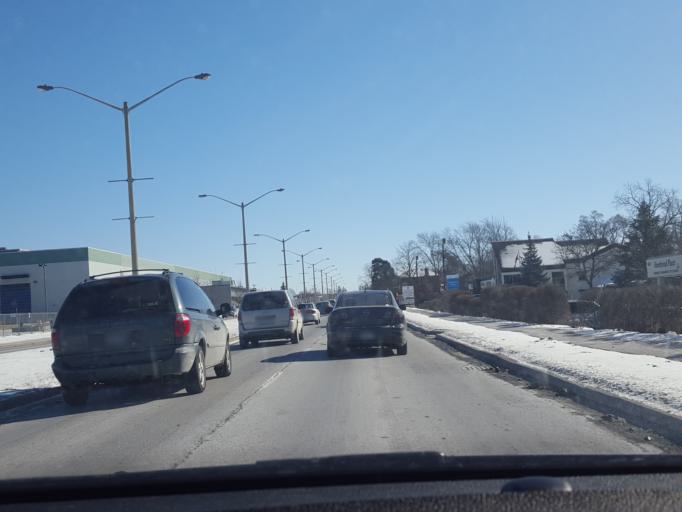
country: CA
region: Ontario
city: Cambridge
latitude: 43.3776
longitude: -80.3259
